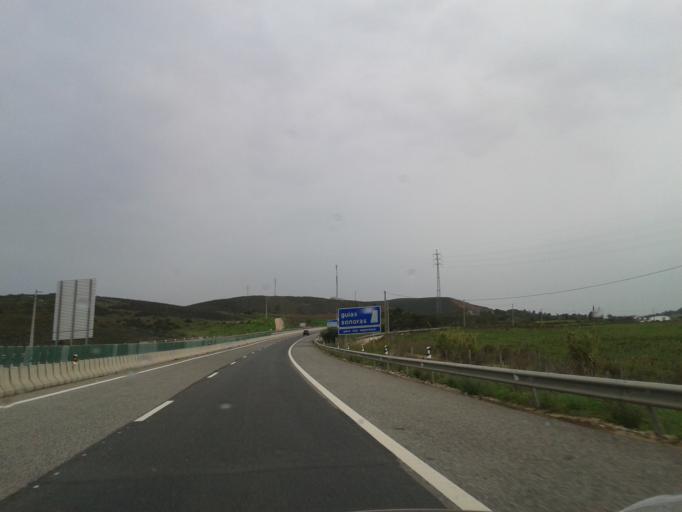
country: PT
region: Faro
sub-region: Lagos
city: Lagos
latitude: 37.1617
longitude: -8.6843
